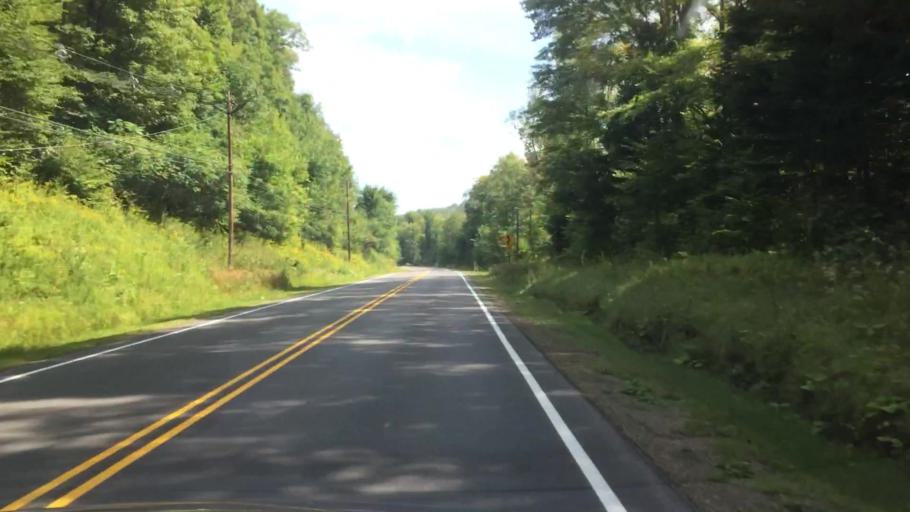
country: US
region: Pennsylvania
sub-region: McKean County
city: Bradford
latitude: 41.8897
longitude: -78.6016
